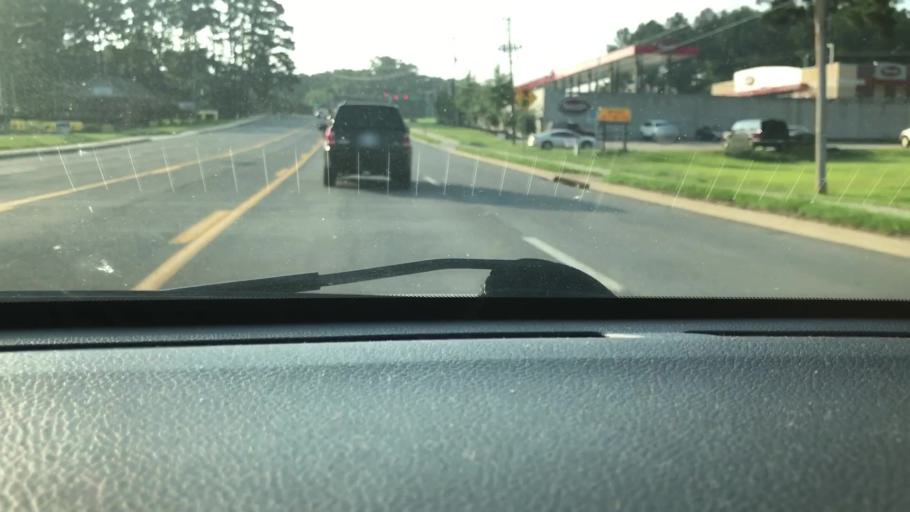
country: US
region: Arkansas
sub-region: Saline County
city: Bryant
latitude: 34.6112
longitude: -92.4952
